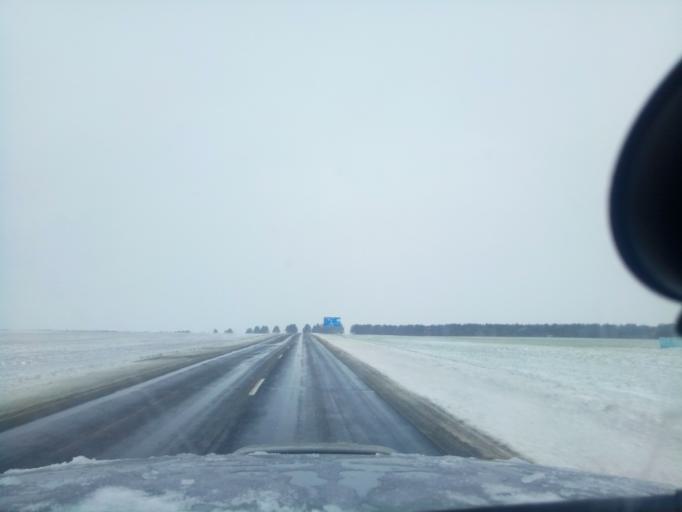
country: BY
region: Minsk
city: Haradzyeya
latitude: 53.2981
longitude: 26.5752
